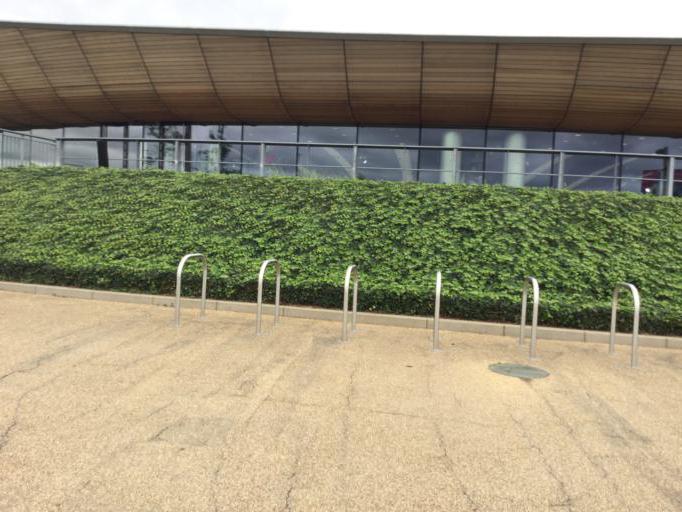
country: GB
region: England
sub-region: Greater London
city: Hackney
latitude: 51.5501
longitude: -0.0163
